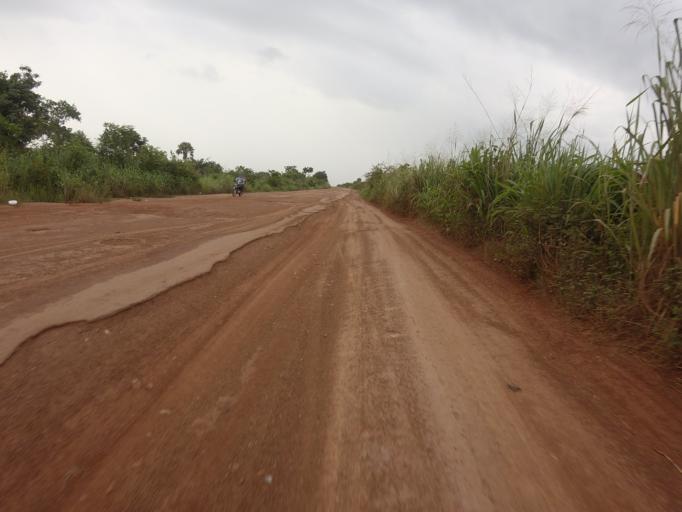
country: GH
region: Volta
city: Kpandu
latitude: 7.0148
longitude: 0.4283
